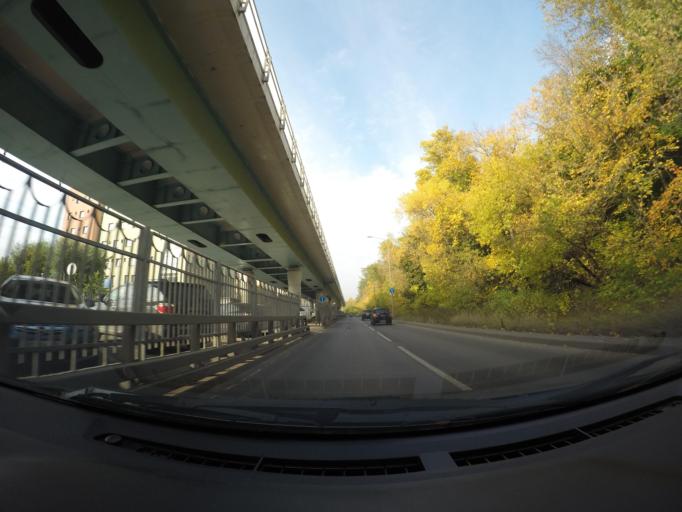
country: RU
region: Moscow
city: Ryazanskiy
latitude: 55.7613
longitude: 37.7526
